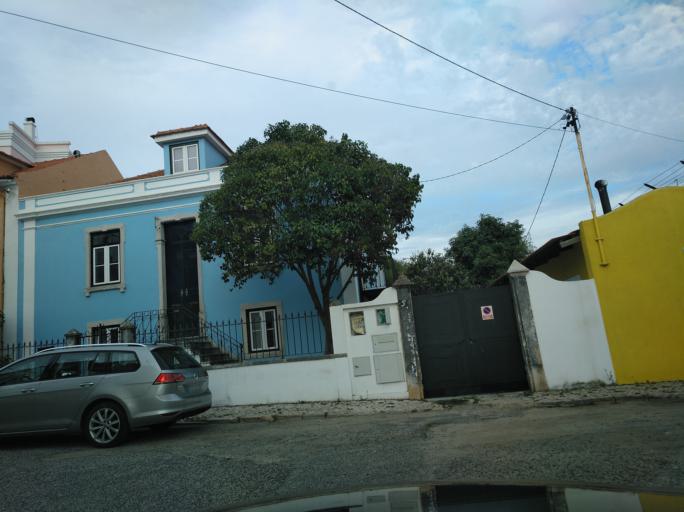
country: PT
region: Lisbon
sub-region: Sintra
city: Queluz
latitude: 38.7524
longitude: -9.2567
